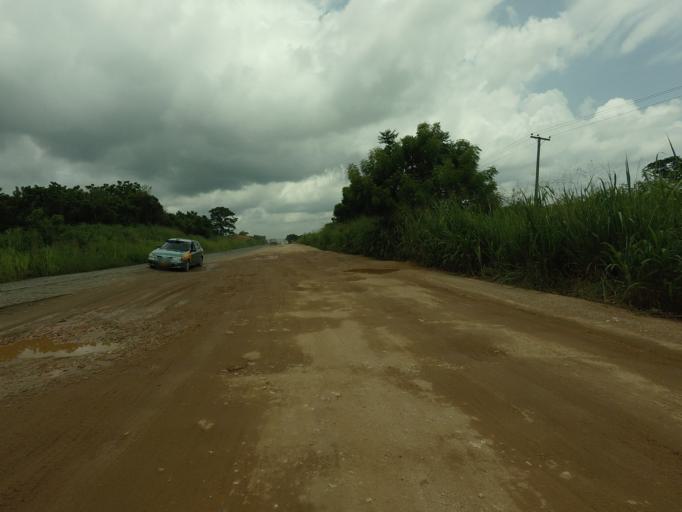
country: GH
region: Volta
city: Ho
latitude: 6.6571
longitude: 0.3034
